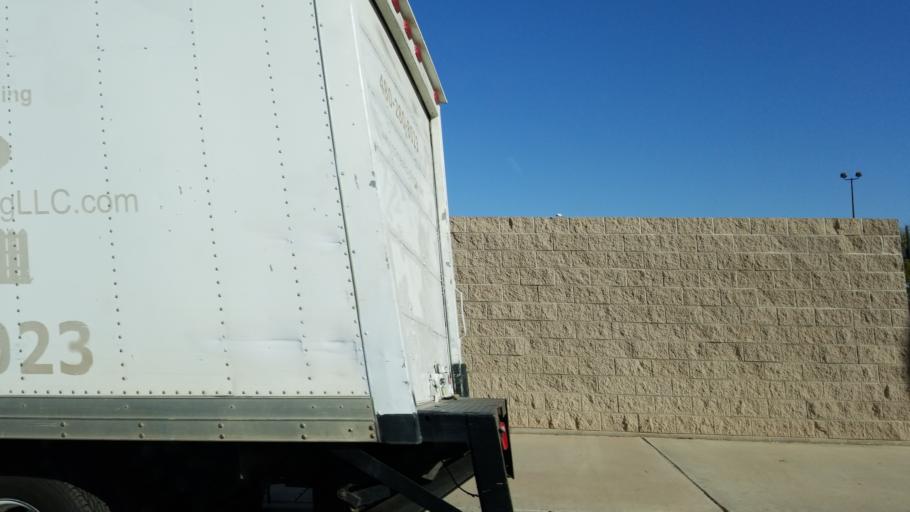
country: US
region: Arizona
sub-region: Maricopa County
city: Phoenix
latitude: 33.4379
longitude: -112.0590
